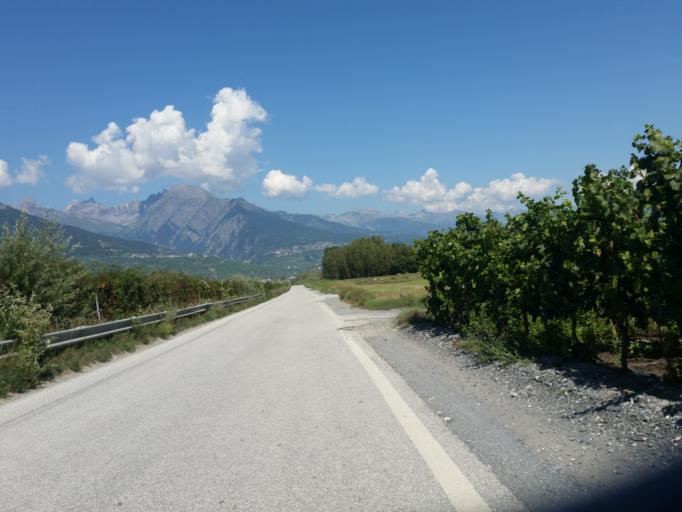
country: CH
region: Valais
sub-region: Conthey District
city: Ardon
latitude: 46.1926
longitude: 7.2494
